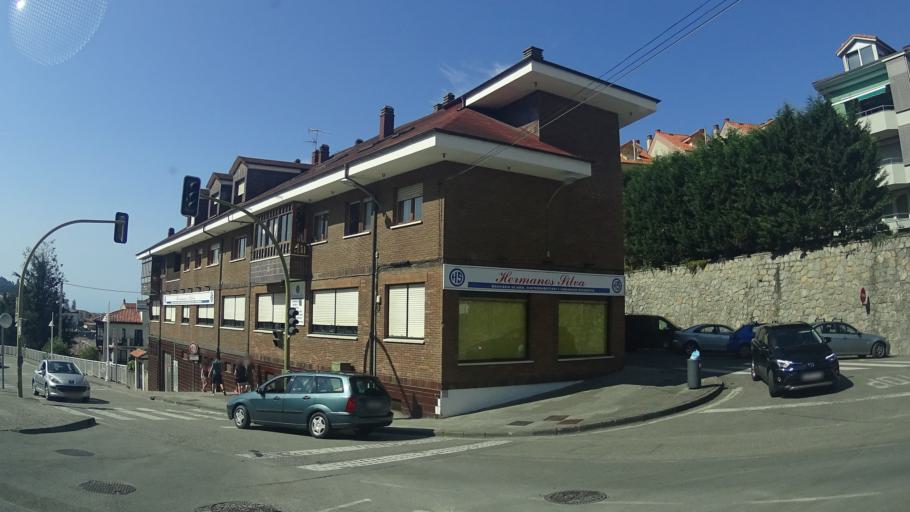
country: ES
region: Asturias
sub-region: Province of Asturias
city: Ribadesella
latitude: 43.4597
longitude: -5.0589
